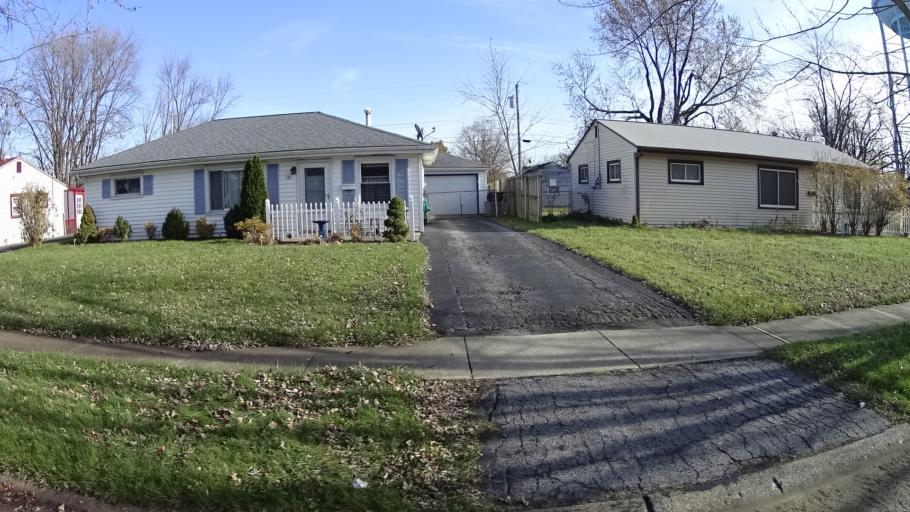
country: US
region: Ohio
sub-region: Lorain County
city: Elyria
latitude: 41.3841
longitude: -82.1125
